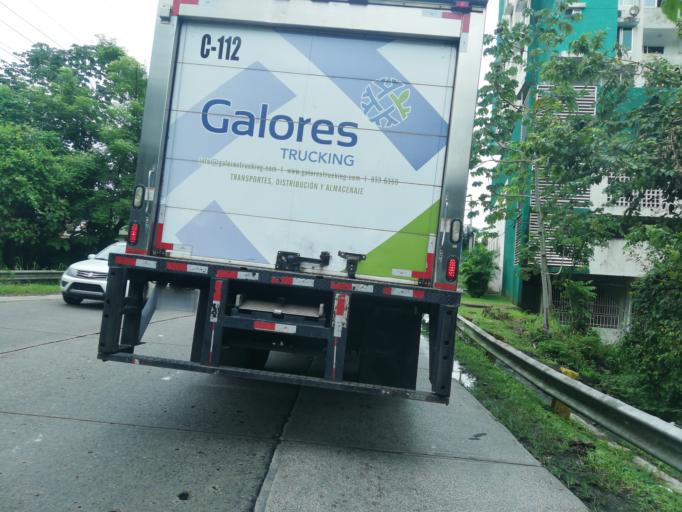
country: PA
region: Panama
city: Panama
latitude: 8.9966
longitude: -79.5401
